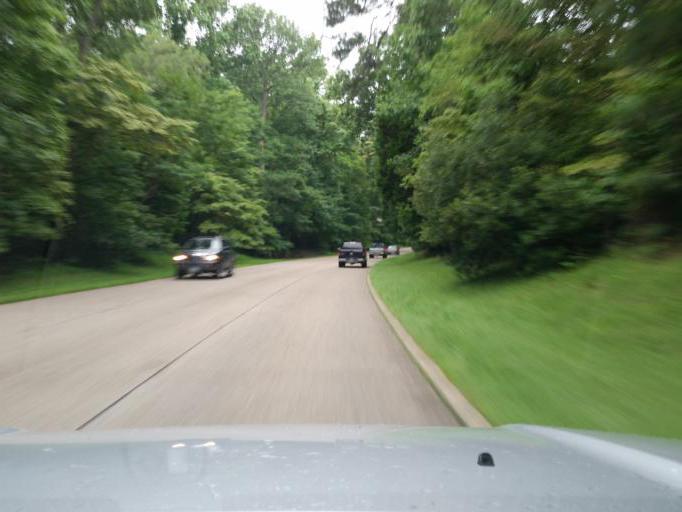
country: US
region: Virginia
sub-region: York County
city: Yorktown
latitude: 37.2717
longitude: -76.5935
